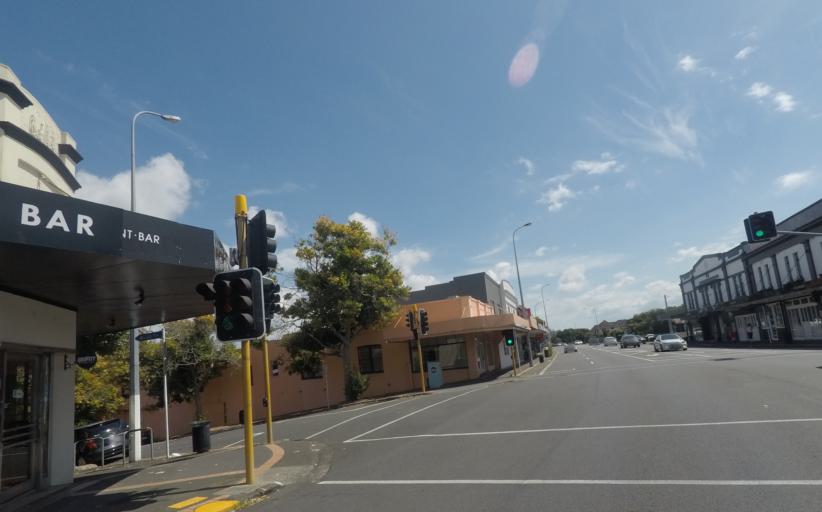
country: NZ
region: Auckland
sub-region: Auckland
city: Auckland
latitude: -36.8804
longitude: 174.8120
